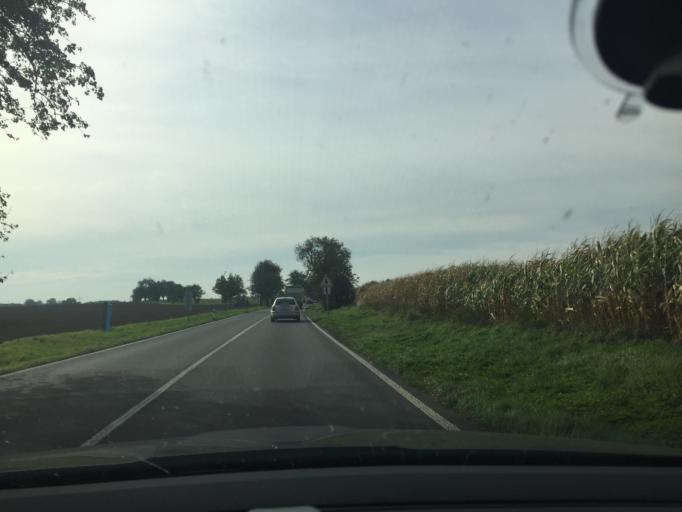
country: CZ
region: Central Bohemia
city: Cirkvice
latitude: 49.9426
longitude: 15.3285
